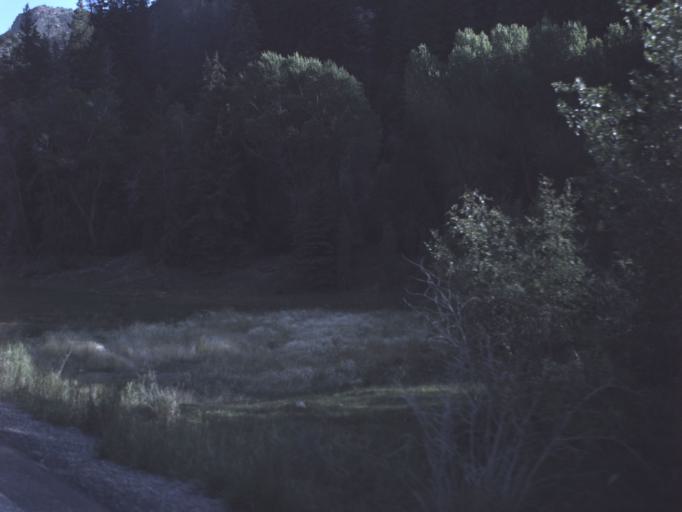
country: US
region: Utah
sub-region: Emery County
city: Huntington
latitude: 39.4562
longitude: -111.1432
